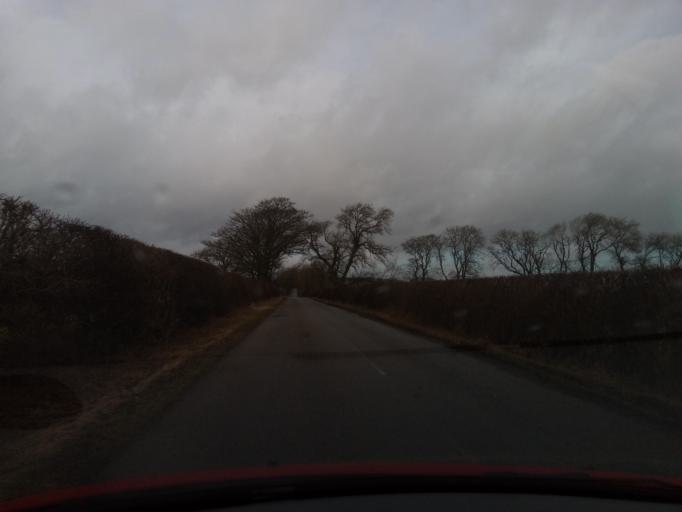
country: GB
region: England
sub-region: Northumberland
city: Rothley
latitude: 55.1806
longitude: -1.9681
